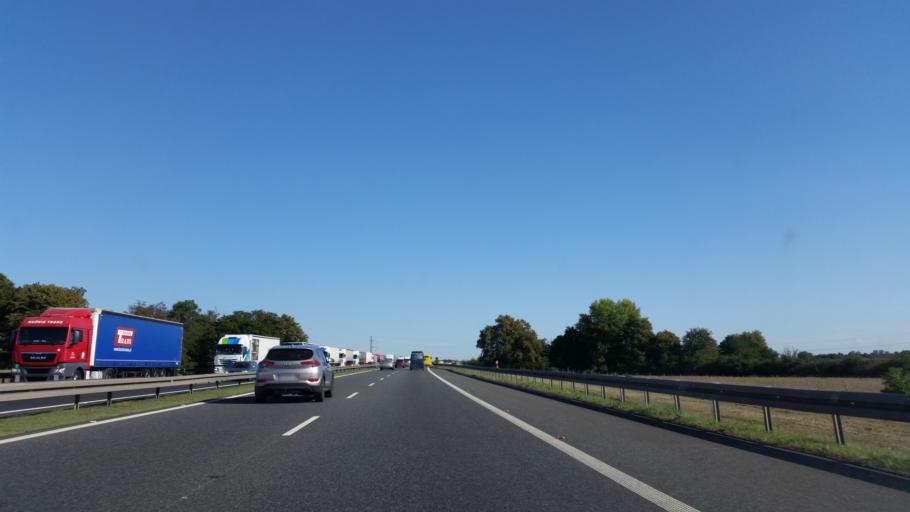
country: PL
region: Lower Silesian Voivodeship
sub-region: Powiat wroclawski
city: Zerniki Wroclawskie
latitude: 51.0200
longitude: 17.0196
